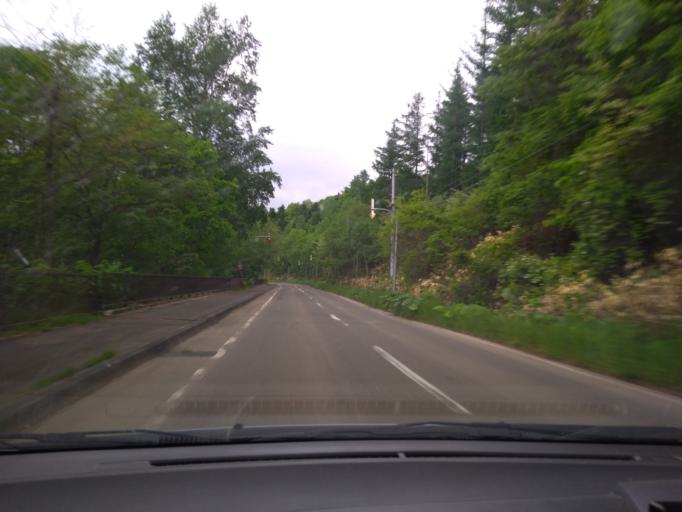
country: JP
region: Hokkaido
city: Shimo-furano
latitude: 43.1749
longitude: 142.5559
